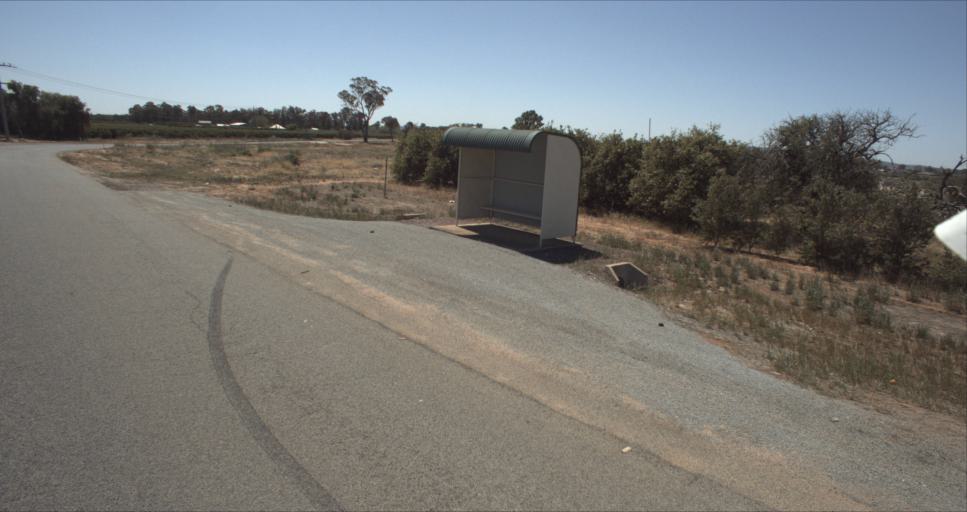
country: AU
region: New South Wales
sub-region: Leeton
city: Leeton
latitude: -34.5383
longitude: 146.3956
